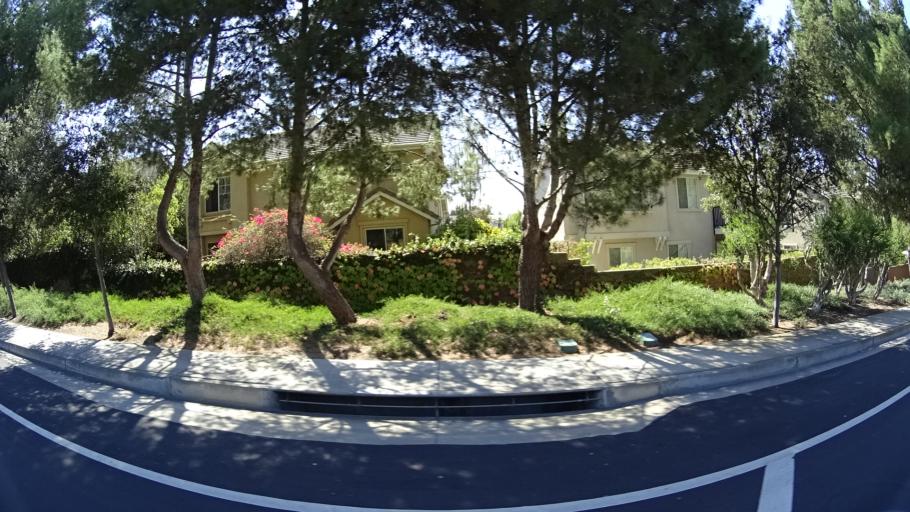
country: US
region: California
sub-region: Orange County
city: San Clemente
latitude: 33.4751
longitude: -117.6191
